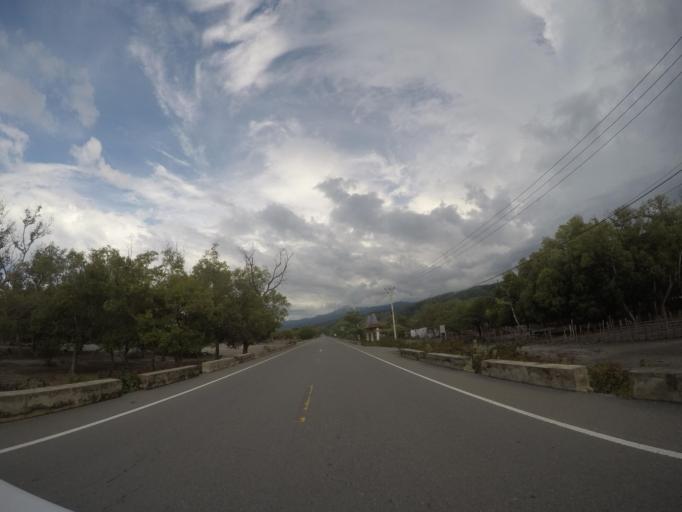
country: TL
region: Liquica
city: Maubara
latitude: -8.6052
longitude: 125.2529
